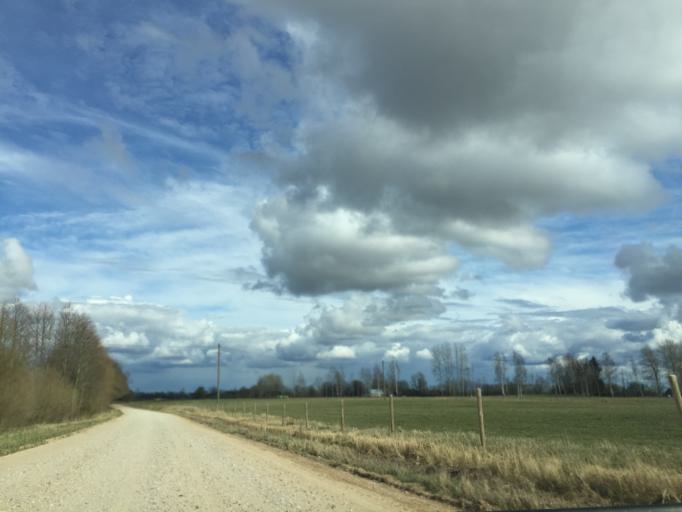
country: LV
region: Limbazu Rajons
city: Limbazi
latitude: 57.6167
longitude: 24.7029
